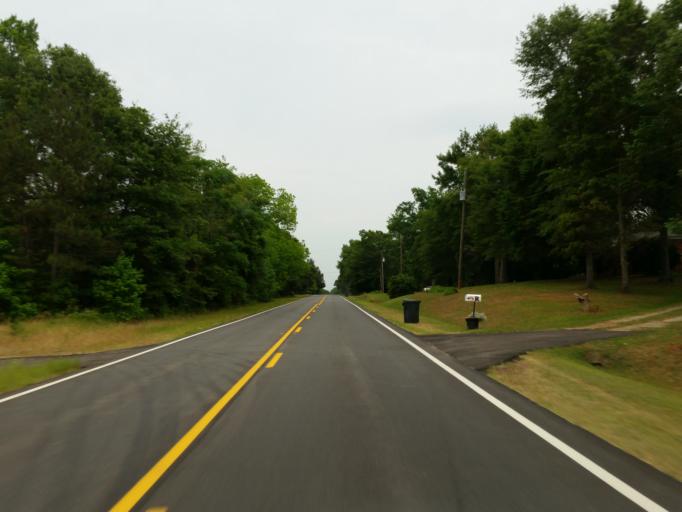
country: US
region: Georgia
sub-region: Dooly County
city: Unadilla
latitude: 32.3280
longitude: -83.7836
